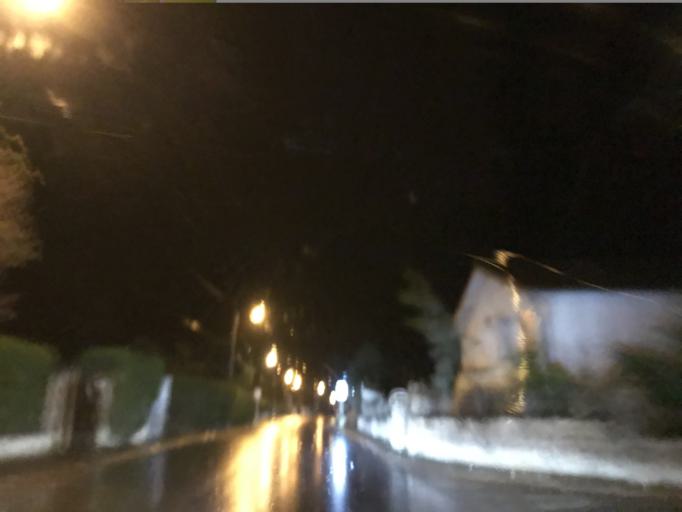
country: FR
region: Auvergne
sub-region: Departement du Puy-de-Dome
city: Celles-sur-Durolle
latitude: 45.8843
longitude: 3.6418
